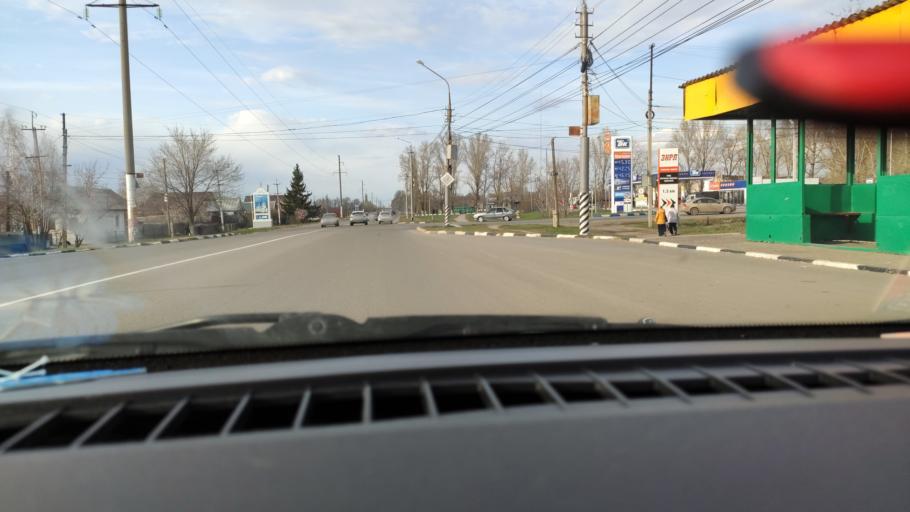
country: RU
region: Saratov
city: Privolzhskiy
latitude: 51.4006
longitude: 46.0362
